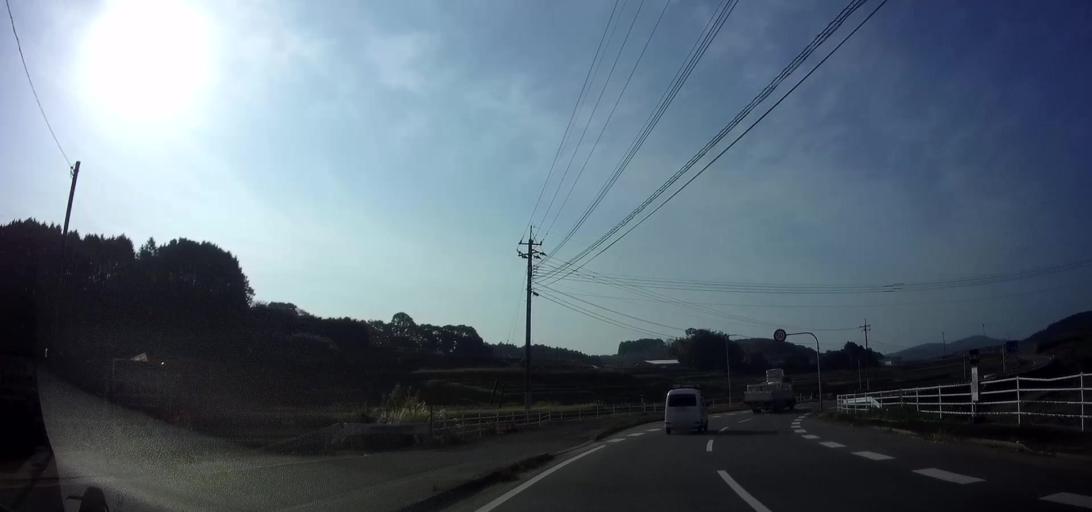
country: JP
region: Nagasaki
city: Shimabara
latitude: 32.6903
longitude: 130.2059
